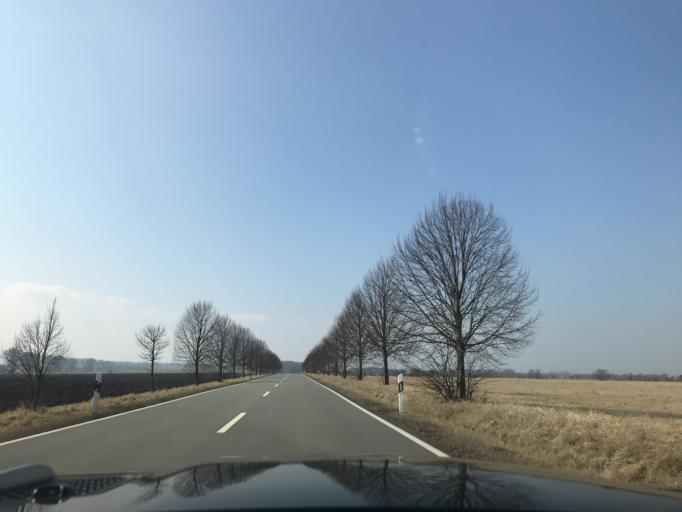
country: DE
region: Thuringia
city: Grossengottern
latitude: 51.1380
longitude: 10.6176
